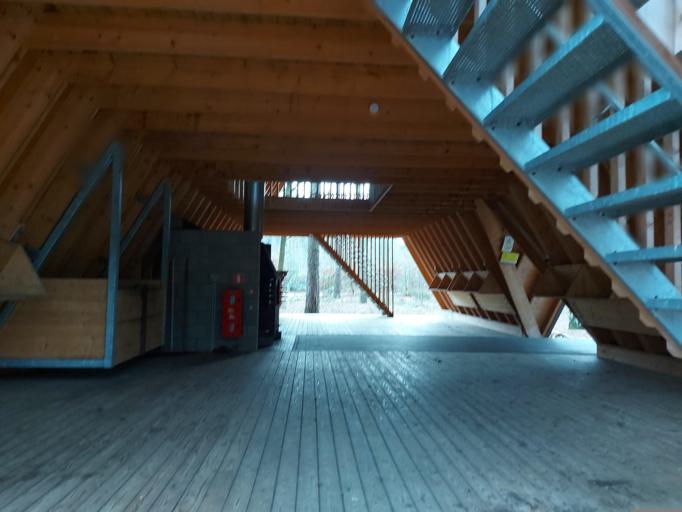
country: BE
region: Flanders
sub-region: Provincie Antwerpen
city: Herentals
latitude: 51.2014
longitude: 4.8519
